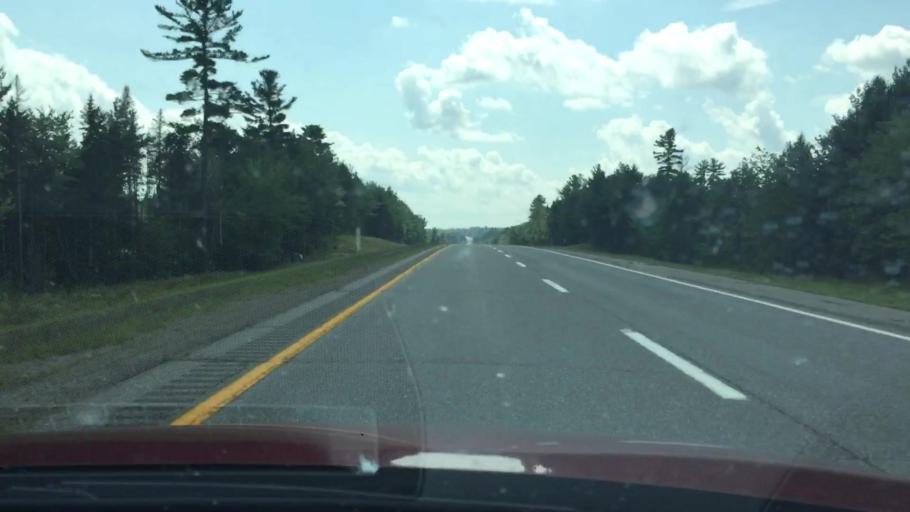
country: US
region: Maine
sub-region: Penobscot County
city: Medway
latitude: 45.4814
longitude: -68.5733
